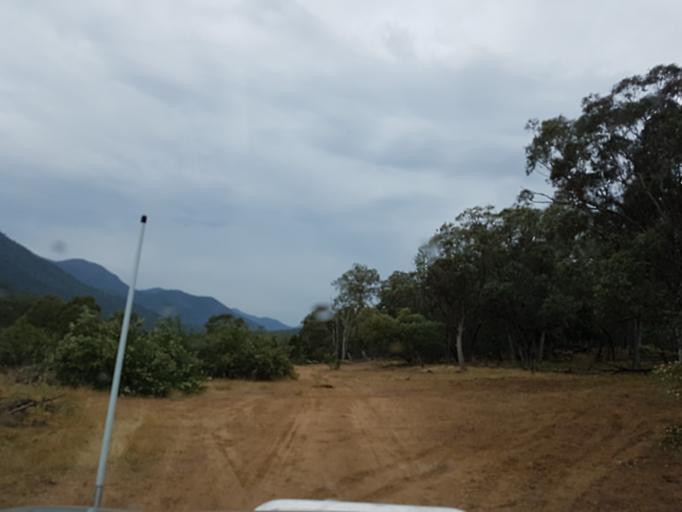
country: AU
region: New South Wales
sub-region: Snowy River
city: Jindabyne
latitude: -36.9460
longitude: 148.3961
